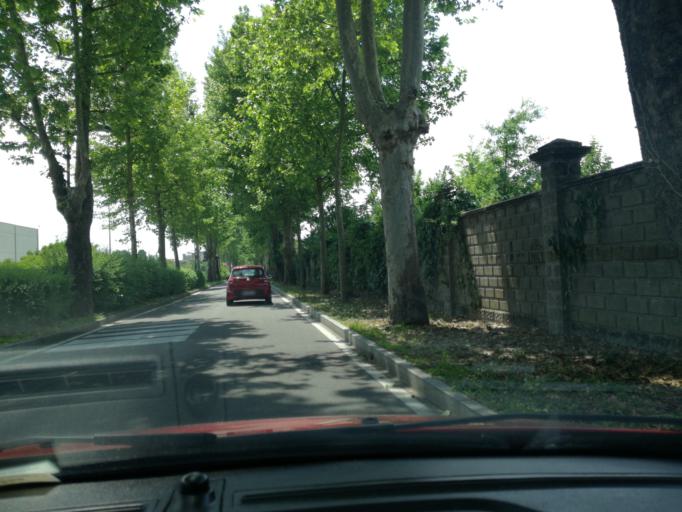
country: IT
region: Lombardy
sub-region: Provincia di Monza e Brianza
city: Limbiate
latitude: 45.6098
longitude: 9.1298
